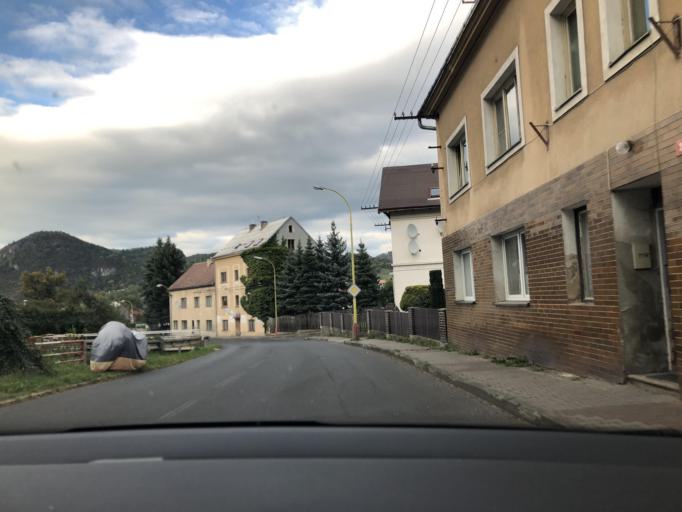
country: CZ
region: Ustecky
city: Velke Brezno
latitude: 50.6604
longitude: 14.1410
